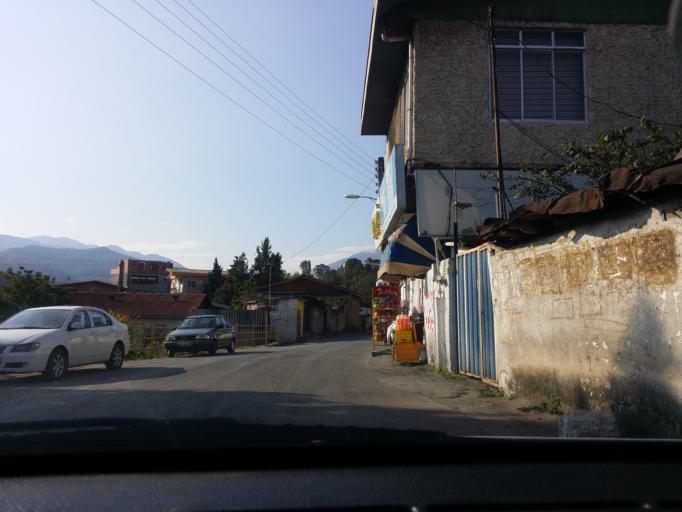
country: IR
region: Mazandaran
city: Chalus
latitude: 36.6503
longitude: 51.4122
